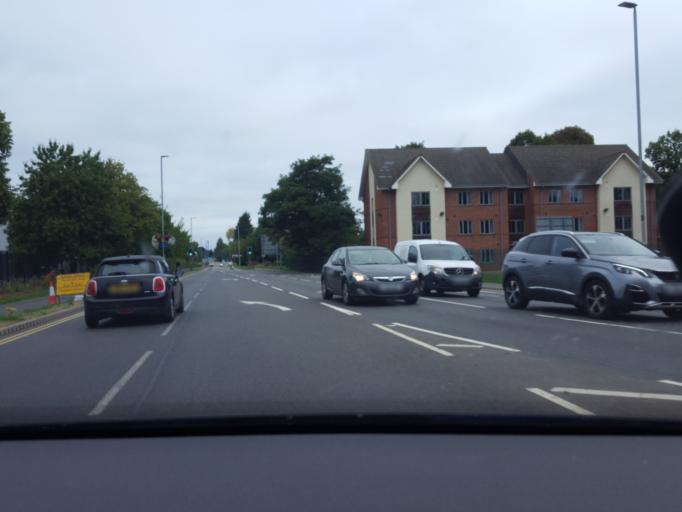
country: GB
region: England
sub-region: Leicestershire
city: Loughborough
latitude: 52.7645
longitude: -1.2186
